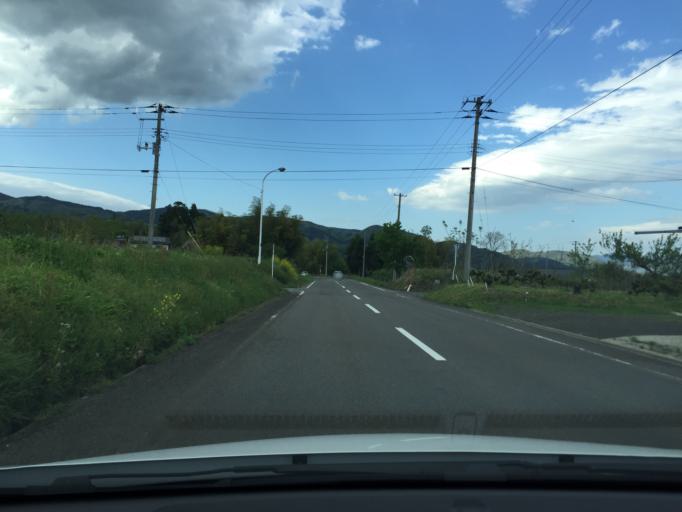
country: JP
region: Fukushima
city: Fukushima-shi
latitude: 37.7532
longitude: 140.3625
